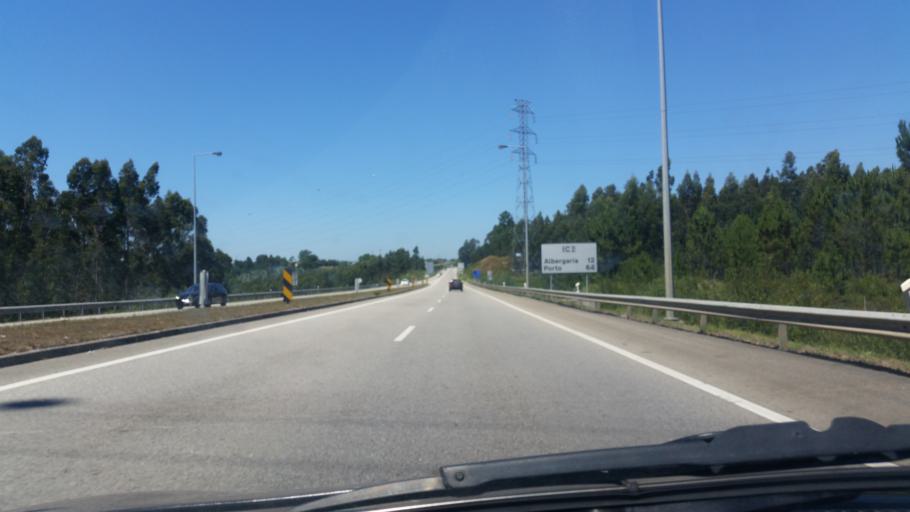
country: PT
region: Aveiro
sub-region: Agueda
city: Valongo
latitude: 40.5989
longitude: -8.4680
